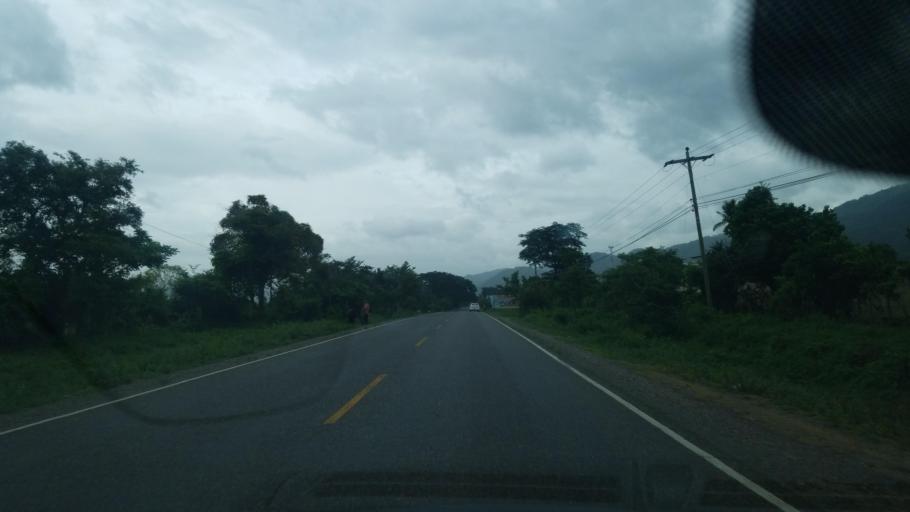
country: HN
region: Ocotepeque
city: Antigua Ocotepeque
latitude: 14.3951
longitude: -89.2008
